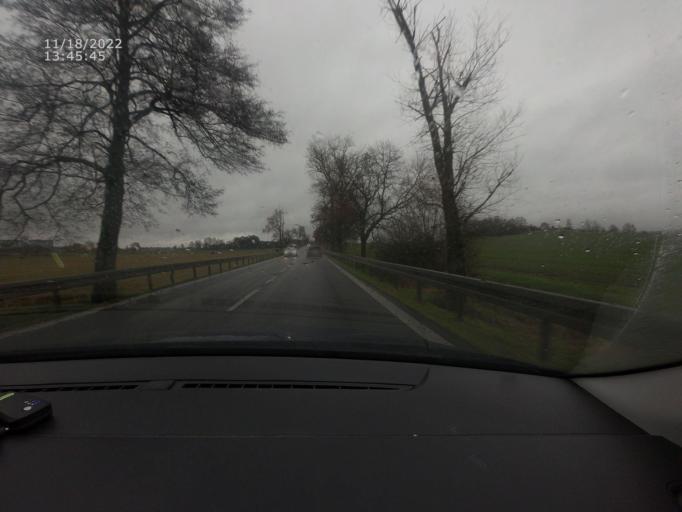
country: CZ
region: Jihocesky
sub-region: Okres Strakonice
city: Blatna
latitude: 49.4272
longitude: 13.8535
